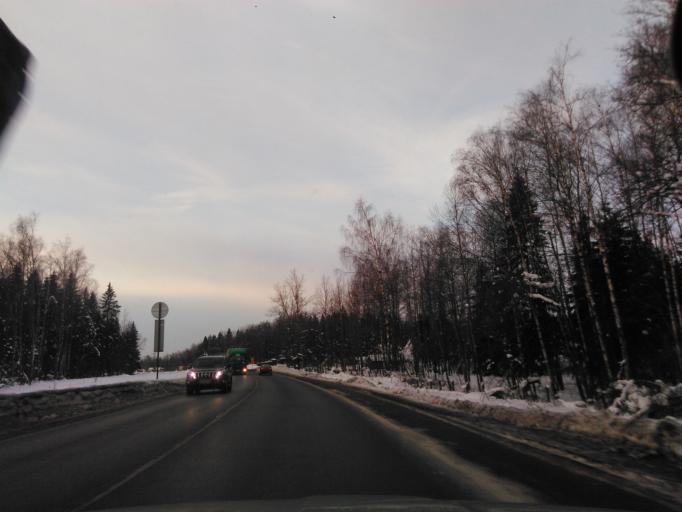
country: RU
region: Moskovskaya
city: Povarovo
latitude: 56.0173
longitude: 37.0305
